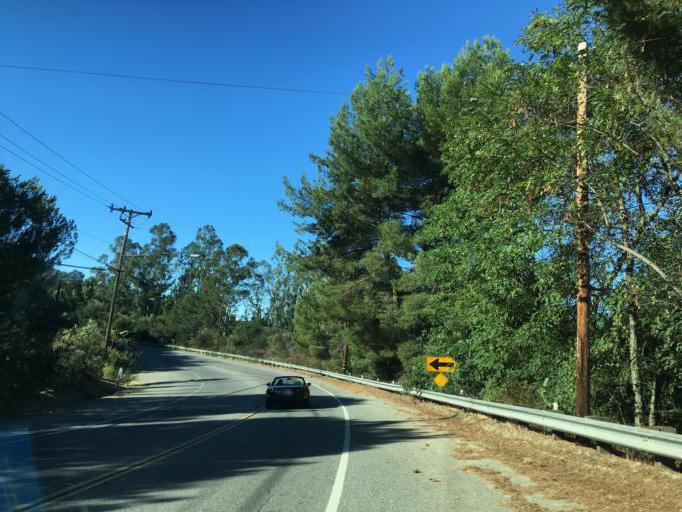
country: US
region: California
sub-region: Los Angeles County
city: Westlake Village
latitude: 34.0931
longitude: -118.8163
